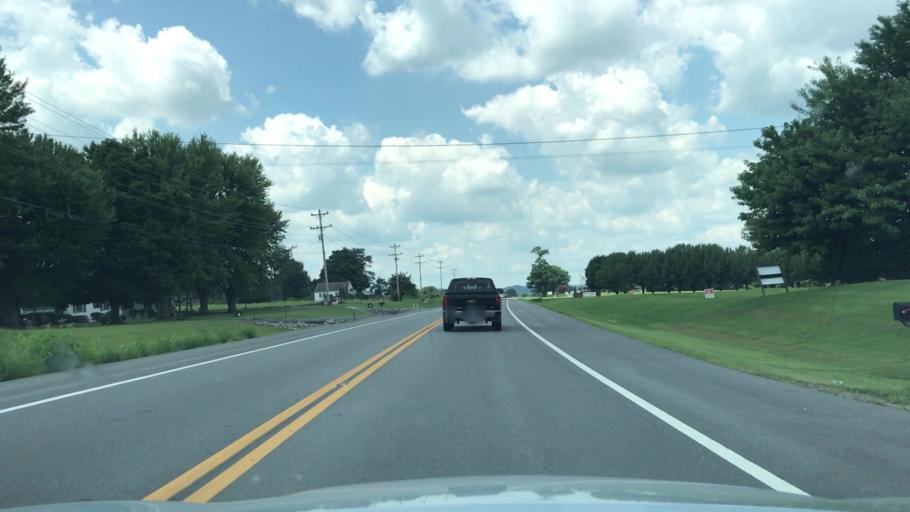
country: US
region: Tennessee
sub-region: Overton County
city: Livingston
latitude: 36.4448
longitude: -85.2215
